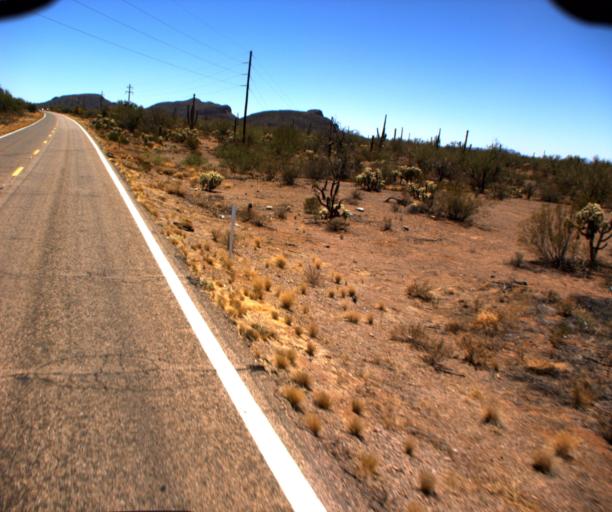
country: US
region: Arizona
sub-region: Pima County
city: Sells
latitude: 31.9861
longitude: -111.9741
